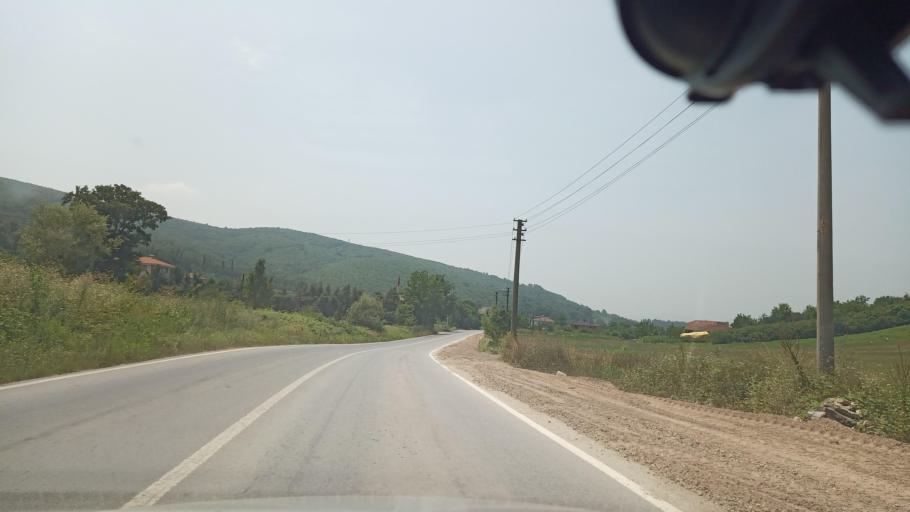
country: TR
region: Sakarya
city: Adapazari
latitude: 40.8399
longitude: 30.4118
